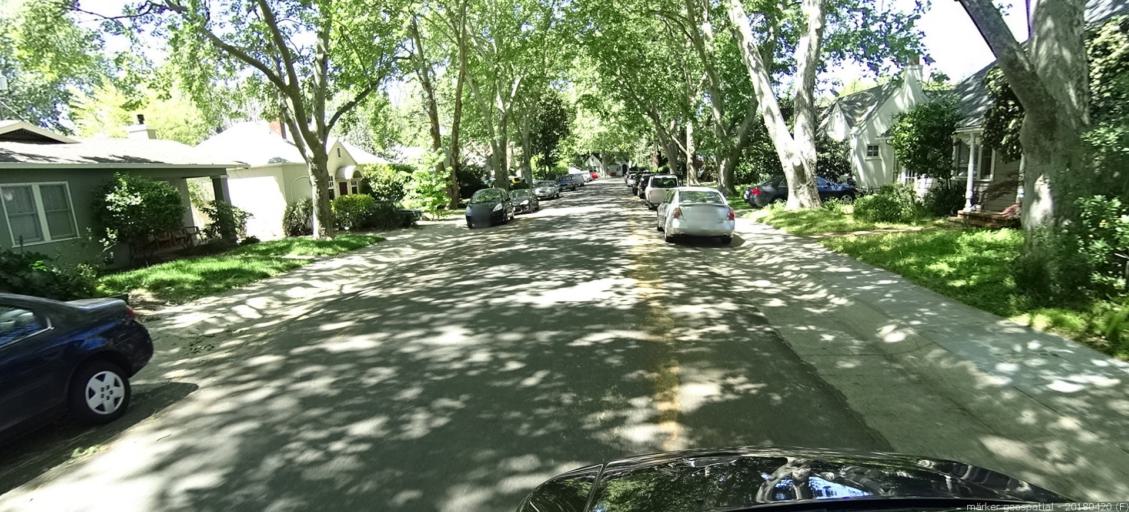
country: US
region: California
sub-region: Sacramento County
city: Sacramento
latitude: 38.5592
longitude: -121.4893
